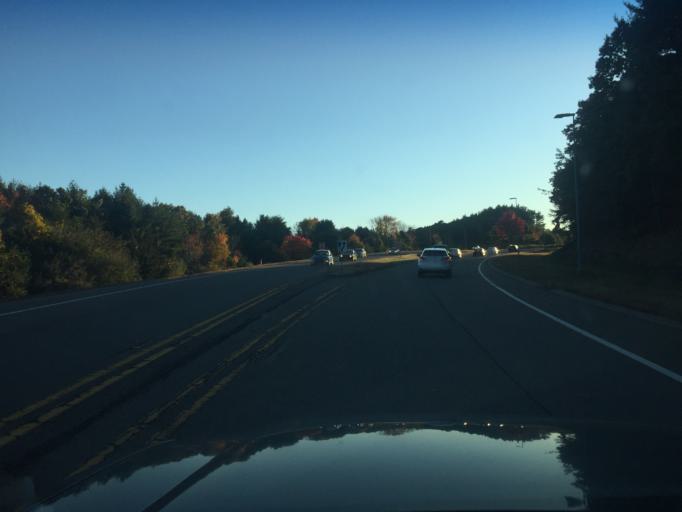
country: US
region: Massachusetts
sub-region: Middlesex County
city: Hudson
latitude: 42.3655
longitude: -71.5806
